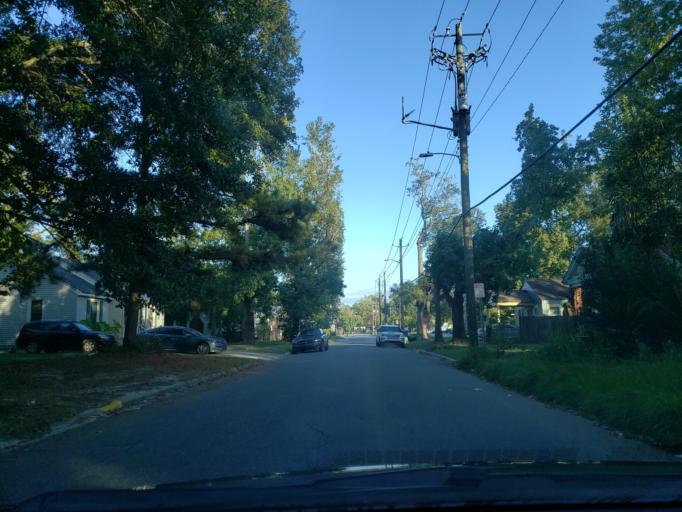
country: US
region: Georgia
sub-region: Chatham County
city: Savannah
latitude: 32.0544
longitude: -81.0855
